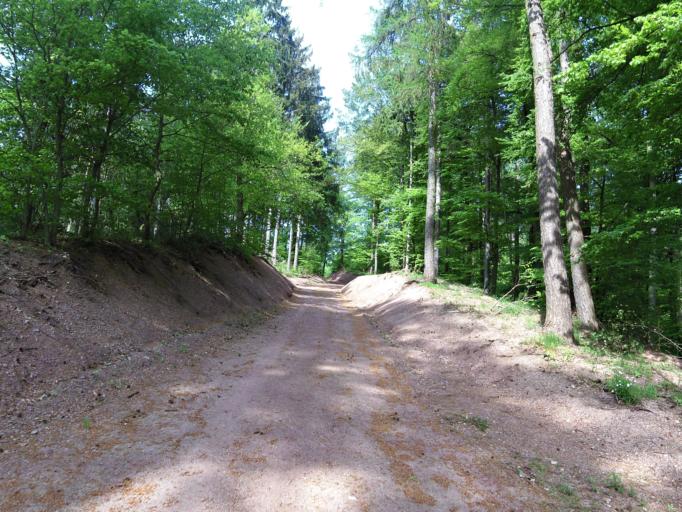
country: DE
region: Thuringia
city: Wolfsburg-Unkeroda
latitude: 50.9445
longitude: 10.2709
